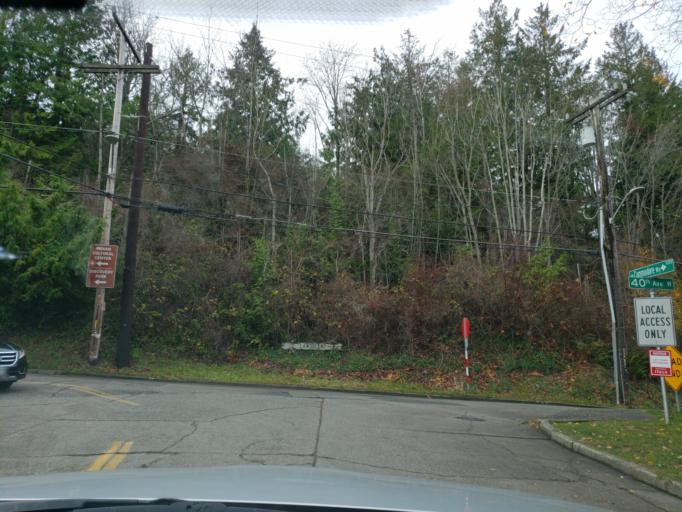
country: US
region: Washington
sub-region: King County
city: Seattle
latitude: 47.6662
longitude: -122.4091
